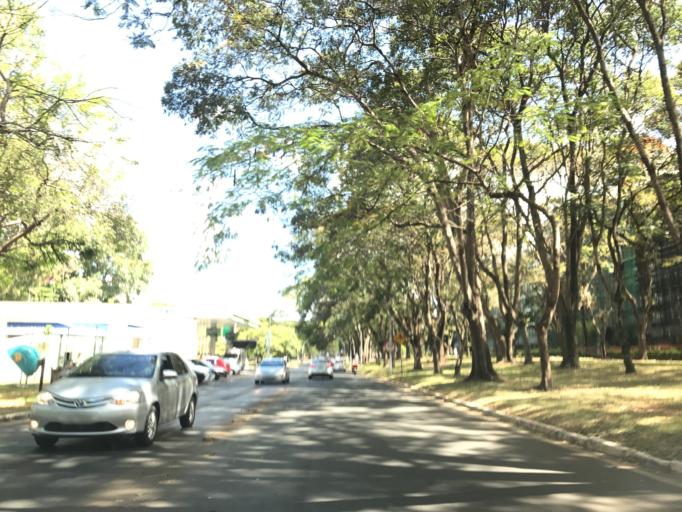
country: BR
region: Federal District
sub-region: Brasilia
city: Brasilia
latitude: -15.8323
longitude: -47.9160
